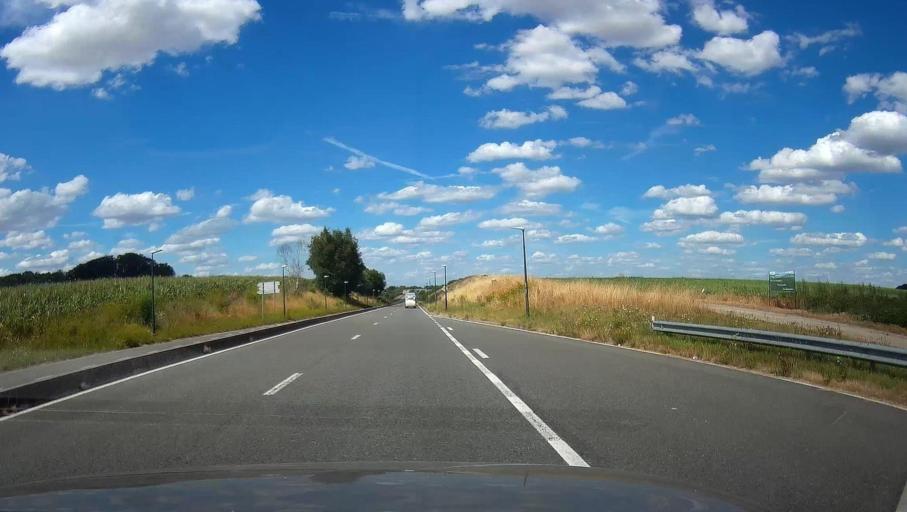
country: BE
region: Wallonia
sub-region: Province du Hainaut
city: Brunehault
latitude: 50.5297
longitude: 4.4589
